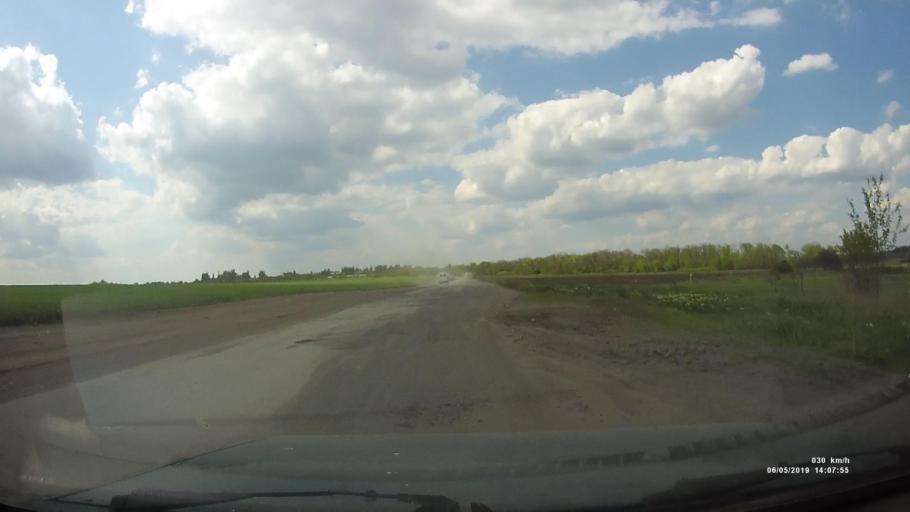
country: RU
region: Rostov
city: Shakhty
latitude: 47.6815
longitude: 40.3011
